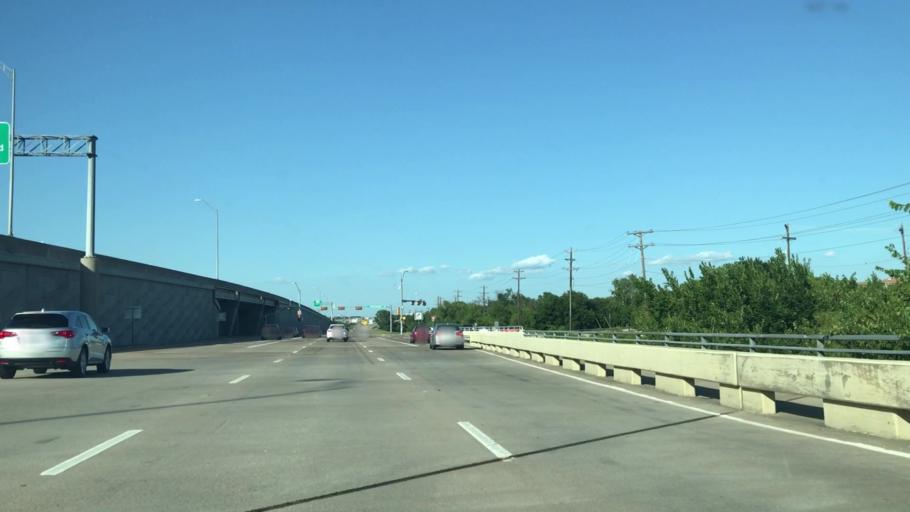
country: US
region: Texas
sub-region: Collin County
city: Frisco
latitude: 33.1180
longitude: -96.7524
